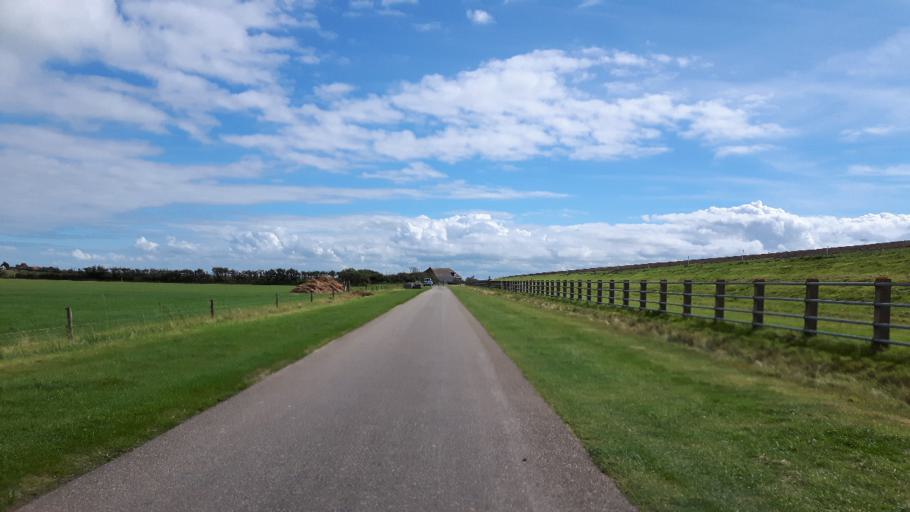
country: NL
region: Friesland
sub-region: Gemeente Ameland
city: Hollum
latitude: 53.4354
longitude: 5.6263
